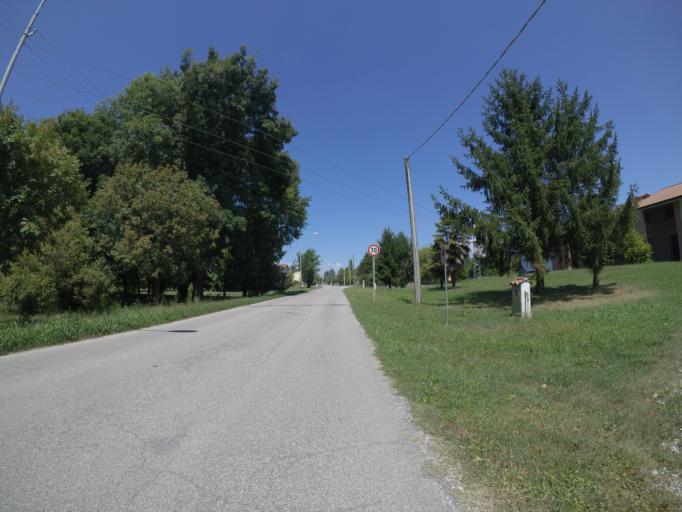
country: IT
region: Friuli Venezia Giulia
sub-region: Provincia di Udine
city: Talmassons
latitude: 45.8848
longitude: 13.1165
